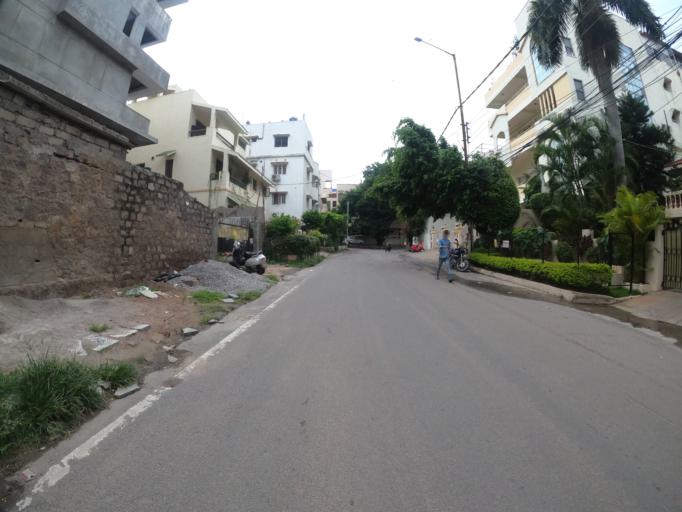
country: IN
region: Telangana
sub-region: Rangareddi
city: Kukatpalli
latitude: 17.4226
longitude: 78.4062
